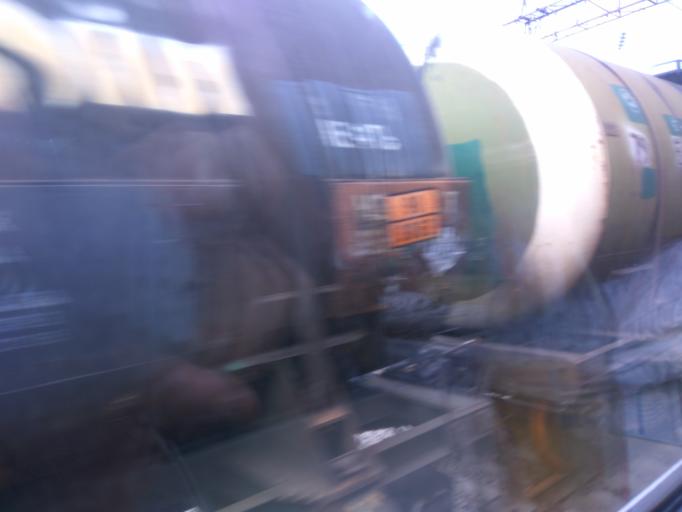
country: RU
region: Saratov
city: Rtishchevo
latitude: 52.2074
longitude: 43.8866
